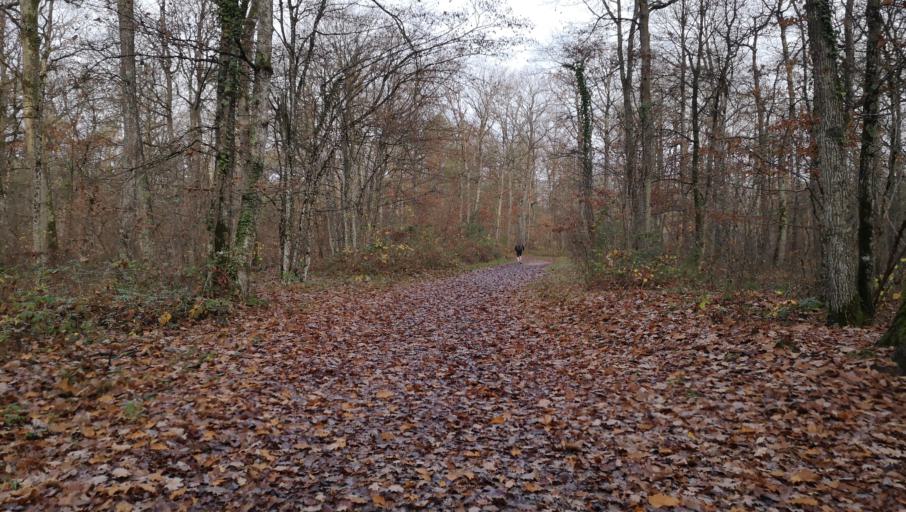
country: FR
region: Centre
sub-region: Departement du Loiret
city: Semoy
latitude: 47.9430
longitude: 1.9601
